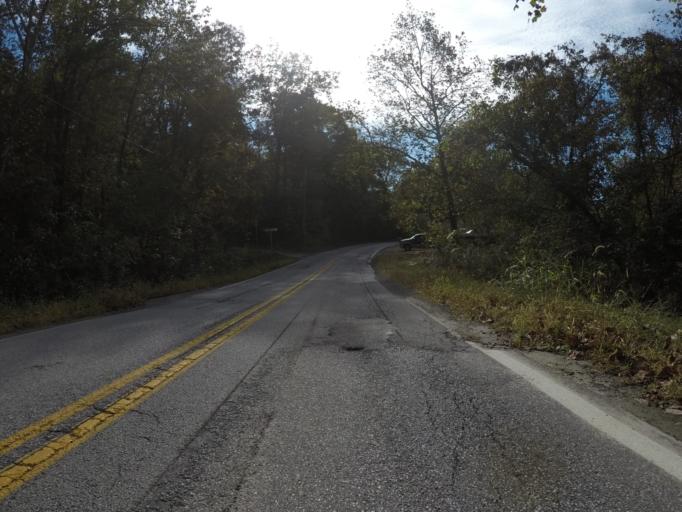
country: US
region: Ohio
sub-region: Lawrence County
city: Burlington
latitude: 38.3657
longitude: -82.5299
